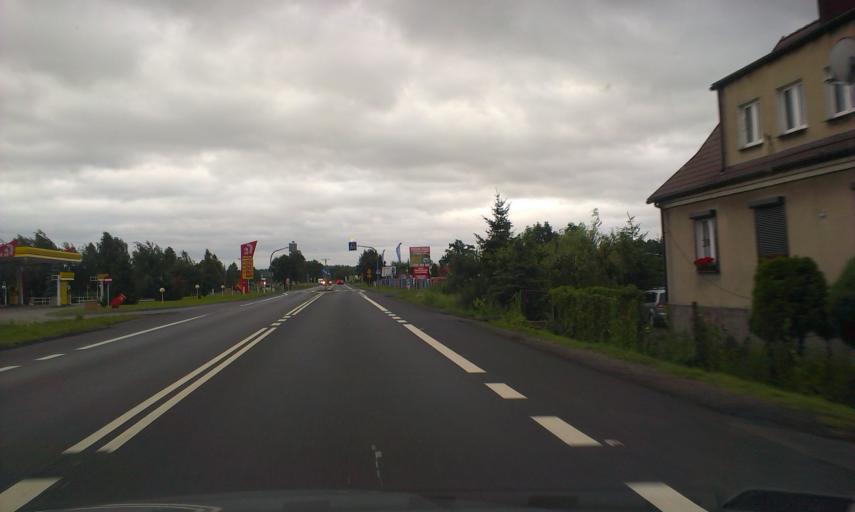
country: PL
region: Greater Poland Voivodeship
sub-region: Powiat pilski
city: Ujscie
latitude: 53.0756
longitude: 16.7314
